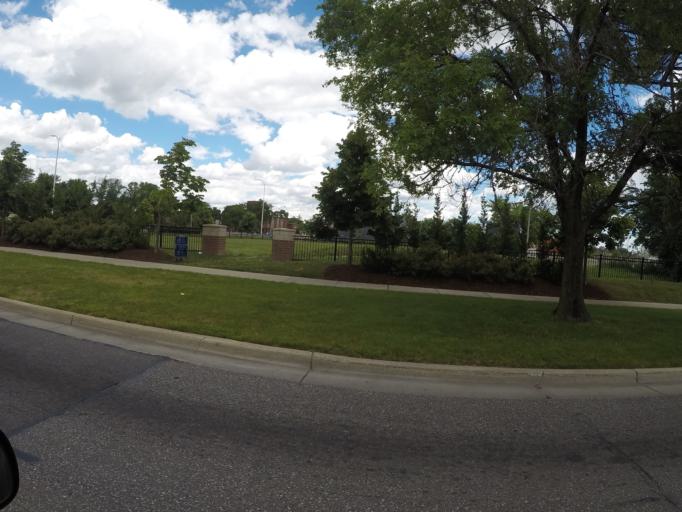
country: US
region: Michigan
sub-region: Oakland County
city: Ferndale
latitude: 42.4459
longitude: -83.1242
